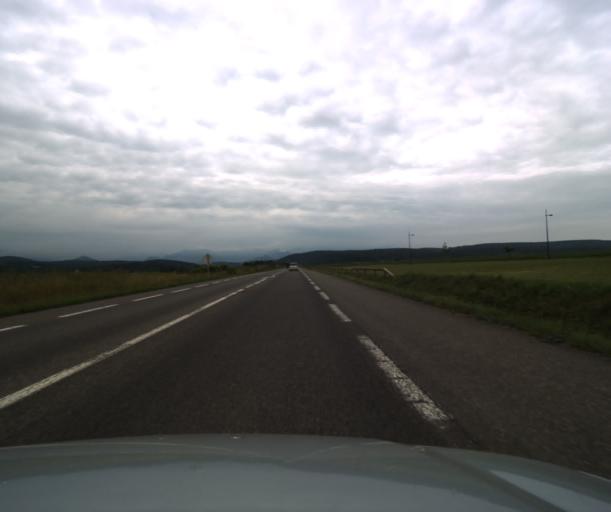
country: FR
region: Midi-Pyrenees
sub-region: Departement des Hautes-Pyrenees
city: Ossun
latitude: 43.1703
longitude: -0.0031
